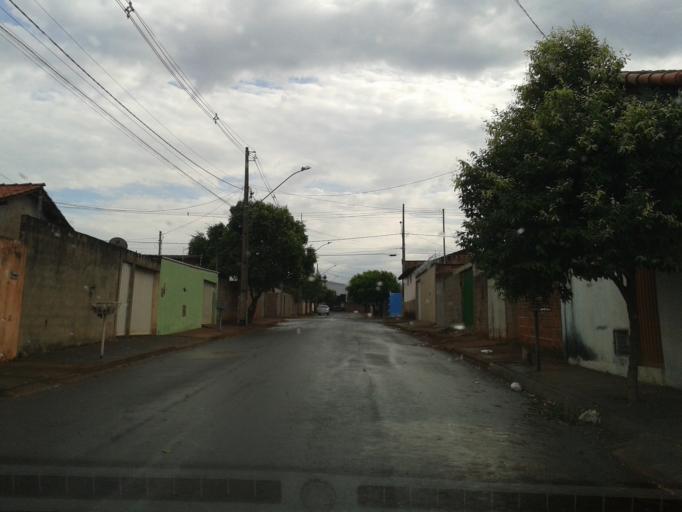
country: BR
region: Minas Gerais
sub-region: Centralina
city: Centralina
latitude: -18.7302
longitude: -49.1991
